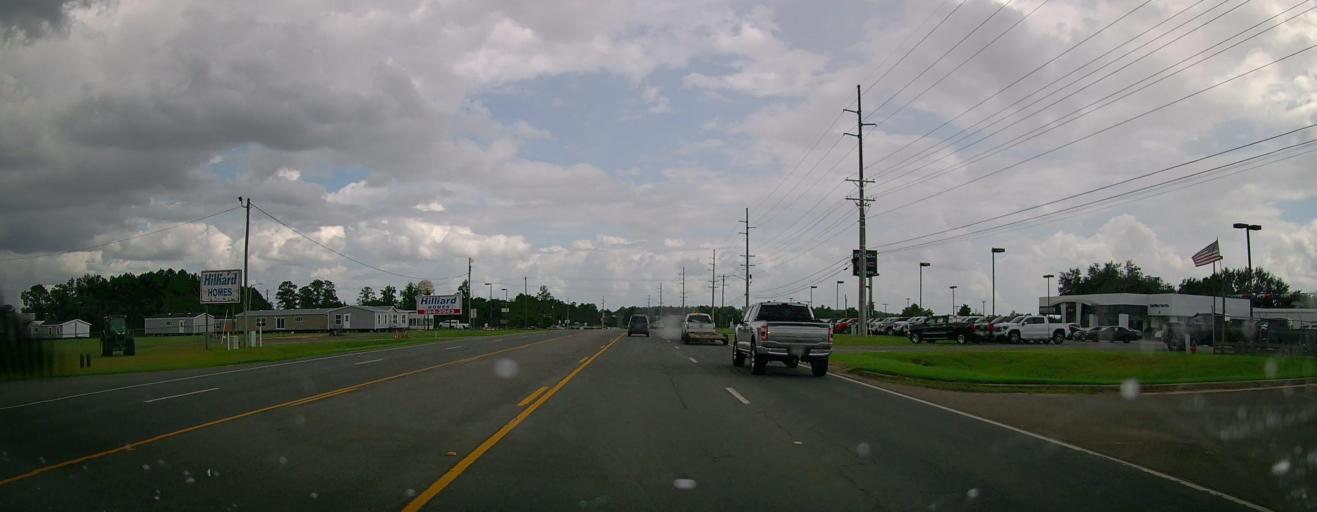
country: US
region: Georgia
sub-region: Coffee County
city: Douglas
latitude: 31.4948
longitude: -82.8717
